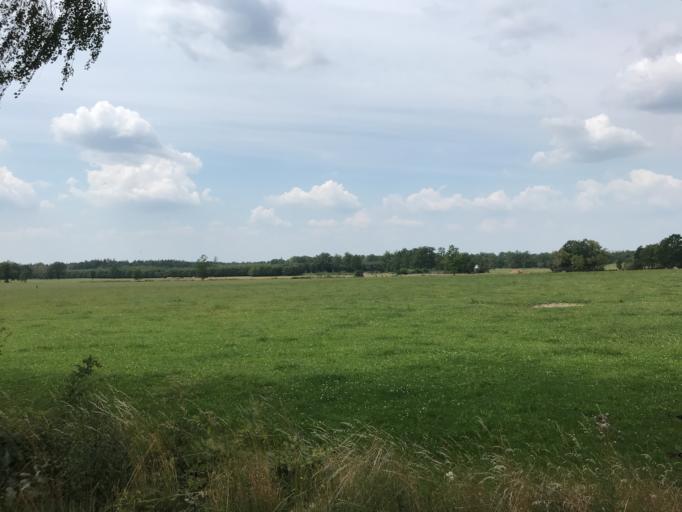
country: CZ
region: Jihocesky
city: Chlum u Trebone
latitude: 49.0231
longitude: 14.8830
